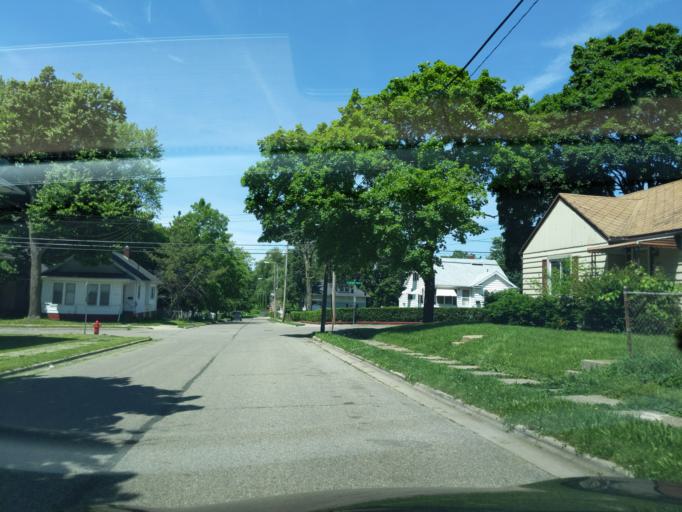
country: US
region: Michigan
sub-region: Ingham County
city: Lansing
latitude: 42.7502
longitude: -84.5354
